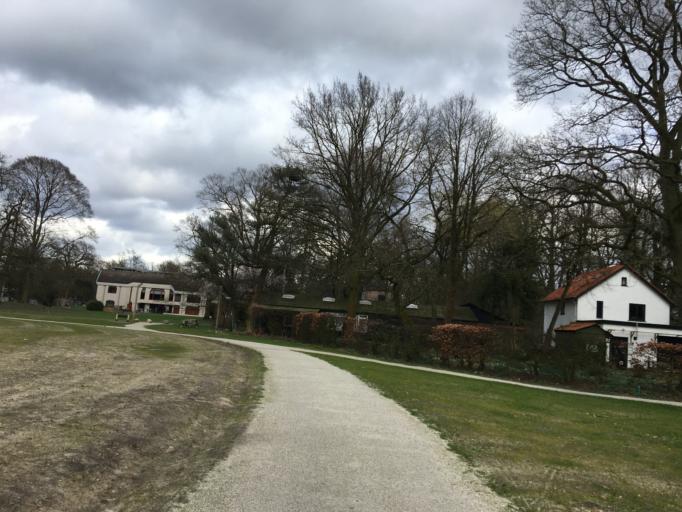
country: NL
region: Utrecht
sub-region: Gemeente Utrechtse Heuvelrug
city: Driebergen-Rijsenburg
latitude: 52.0630
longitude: 5.2601
